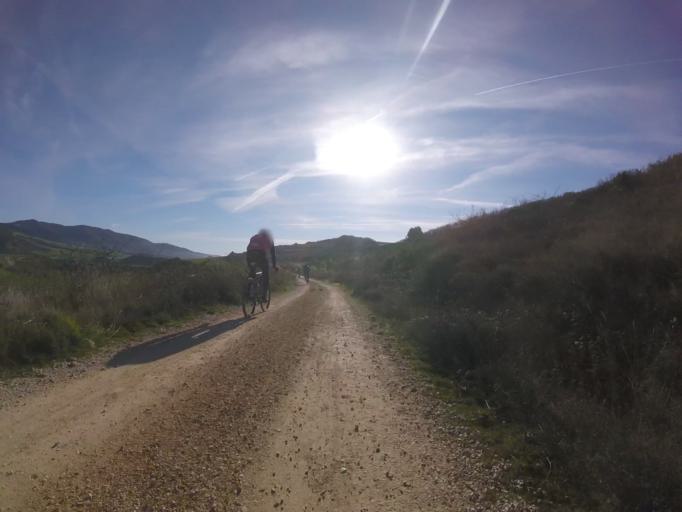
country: ES
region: Navarre
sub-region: Provincia de Navarra
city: Yerri
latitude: 42.6864
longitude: -1.9578
